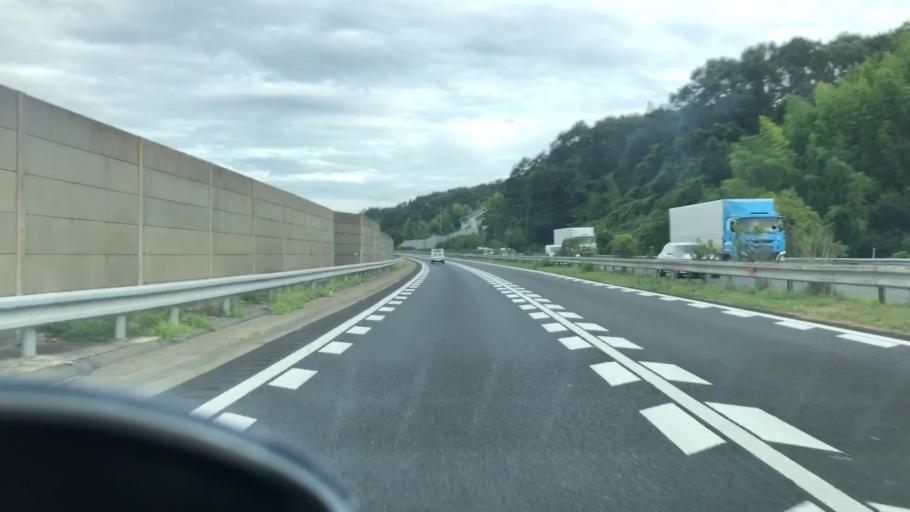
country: JP
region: Hyogo
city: Yashiro
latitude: 34.9005
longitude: 135.0700
